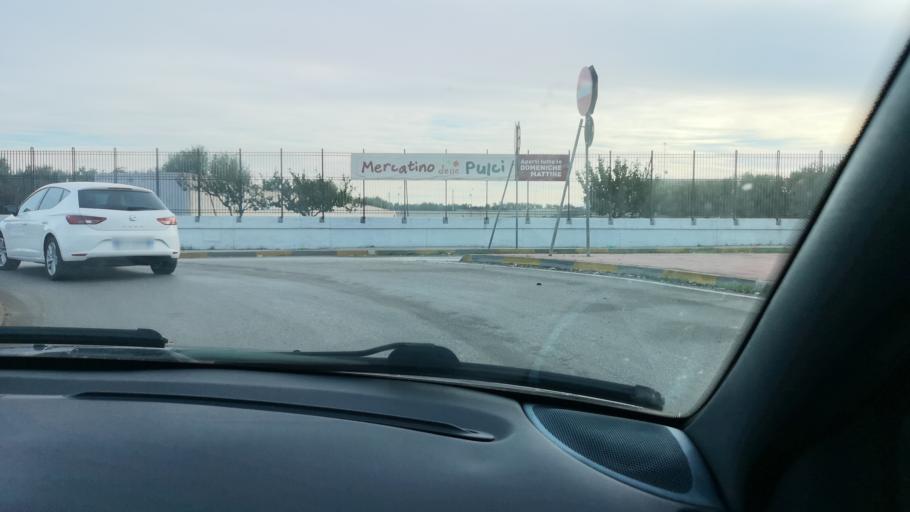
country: IT
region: Apulia
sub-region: Provincia di Bari
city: Sannicandro di Bari
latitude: 40.9919
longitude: 16.8010
